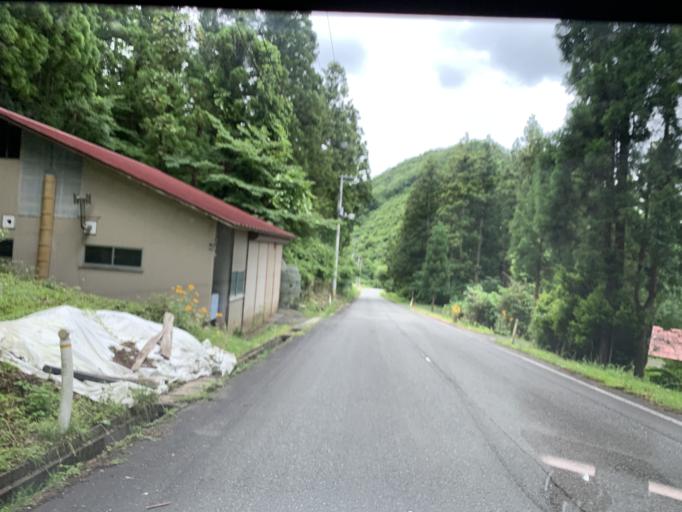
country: JP
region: Iwate
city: Ichinoseki
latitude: 38.8908
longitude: 140.9816
